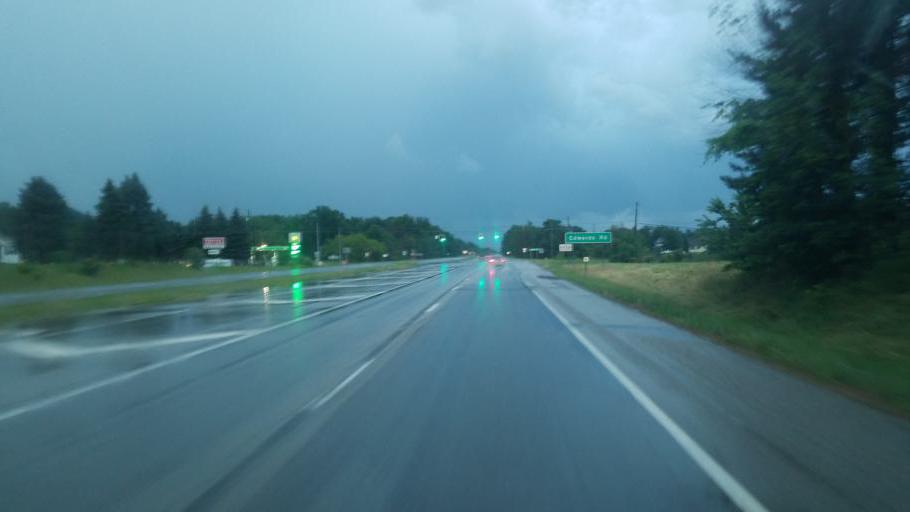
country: US
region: Ohio
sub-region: Wayne County
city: Doylestown
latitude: 40.9618
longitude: -81.6598
